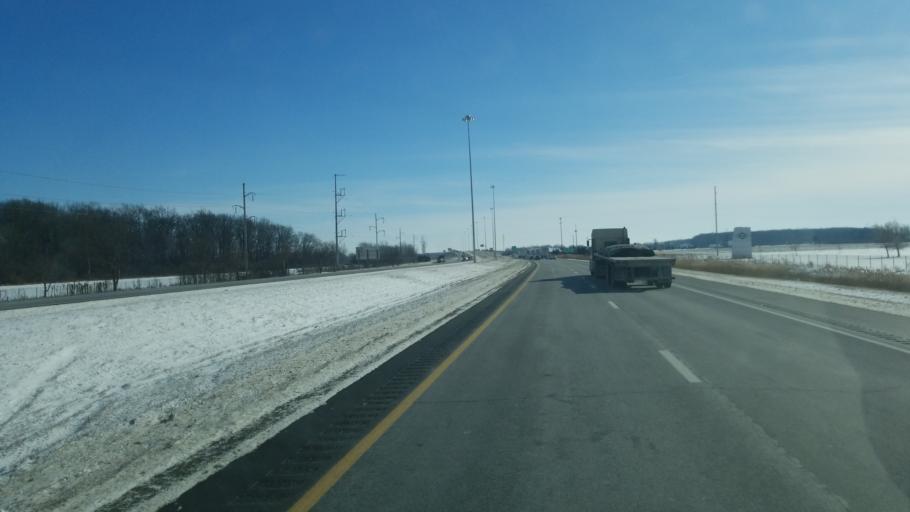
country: US
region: Ohio
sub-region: Lucas County
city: Maumee
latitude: 41.5688
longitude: -83.6911
